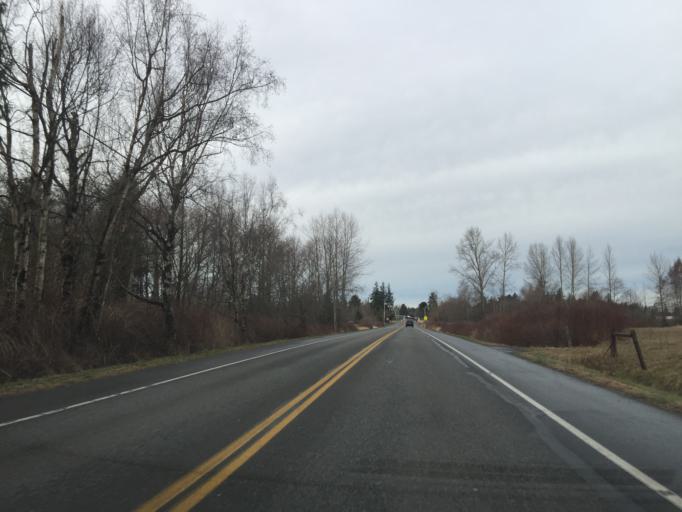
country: US
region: Washington
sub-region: Whatcom County
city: Marietta-Alderwood
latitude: 48.8276
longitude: -122.5365
